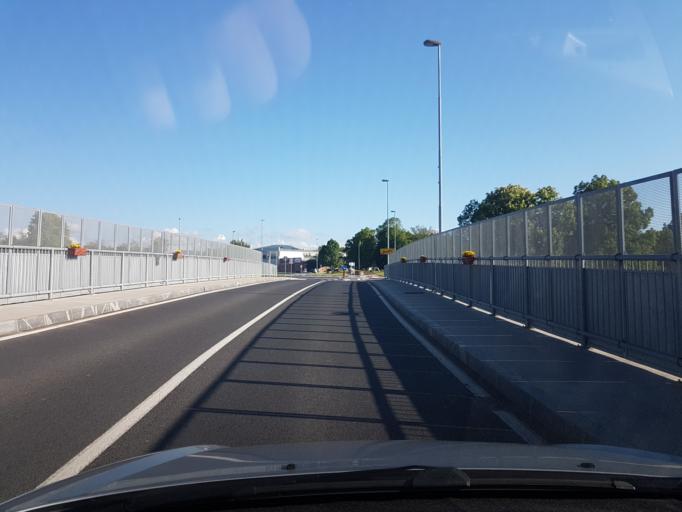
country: SI
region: Divaca
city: Divaca
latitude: 45.6807
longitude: 13.9705
